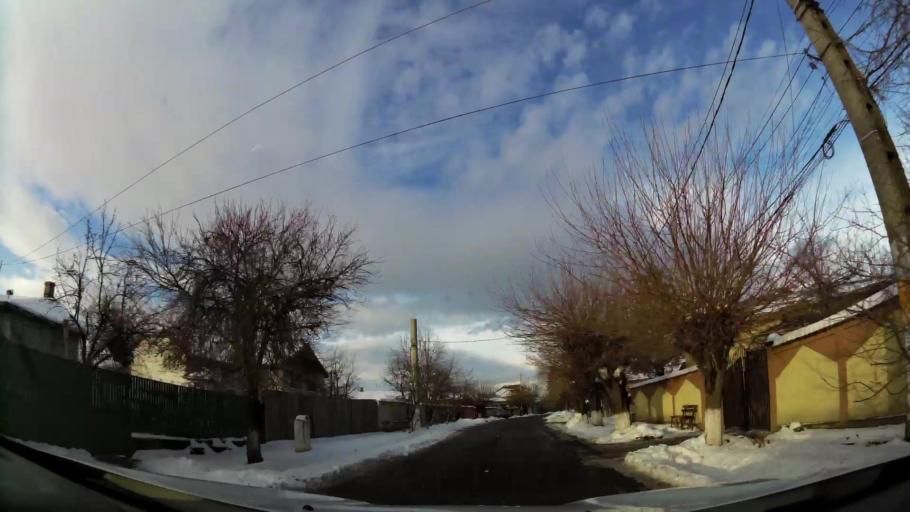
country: RO
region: Ilfov
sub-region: Comuna Jilava
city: Jilava
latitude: 44.3332
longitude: 26.0811
